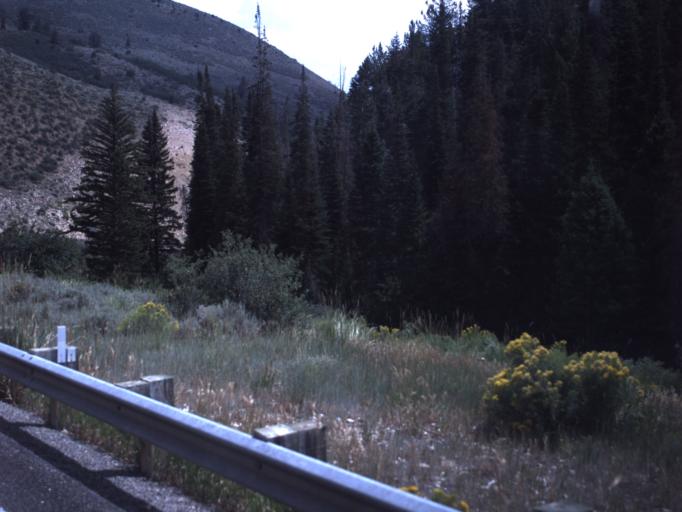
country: US
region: Utah
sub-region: Summit County
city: Francis
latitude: 40.4732
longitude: -110.9125
